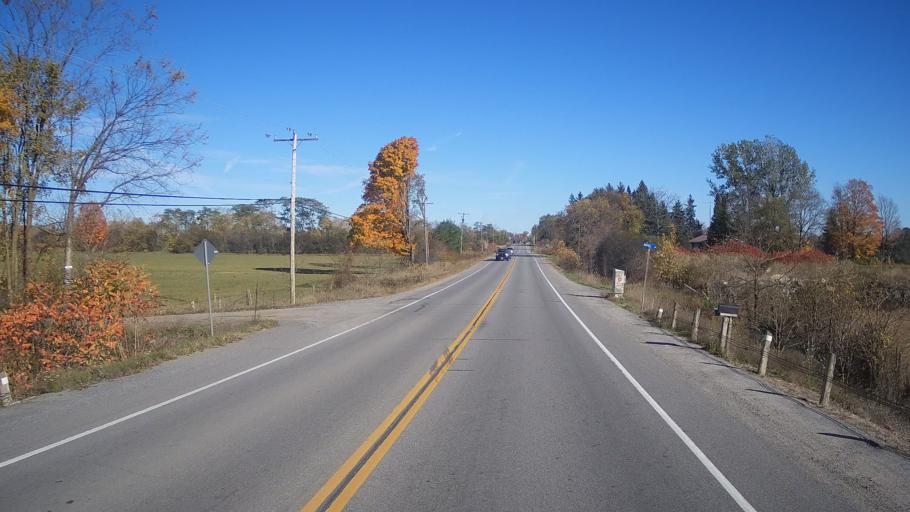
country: CA
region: Ontario
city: Kingston
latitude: 44.4073
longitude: -76.5713
